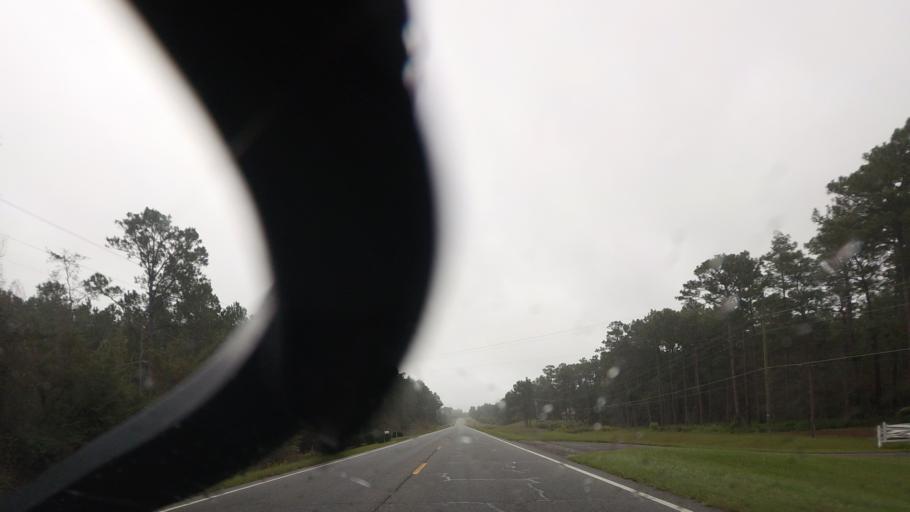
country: US
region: Georgia
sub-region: Ben Hill County
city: Fitzgerald
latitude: 31.7576
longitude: -83.2457
